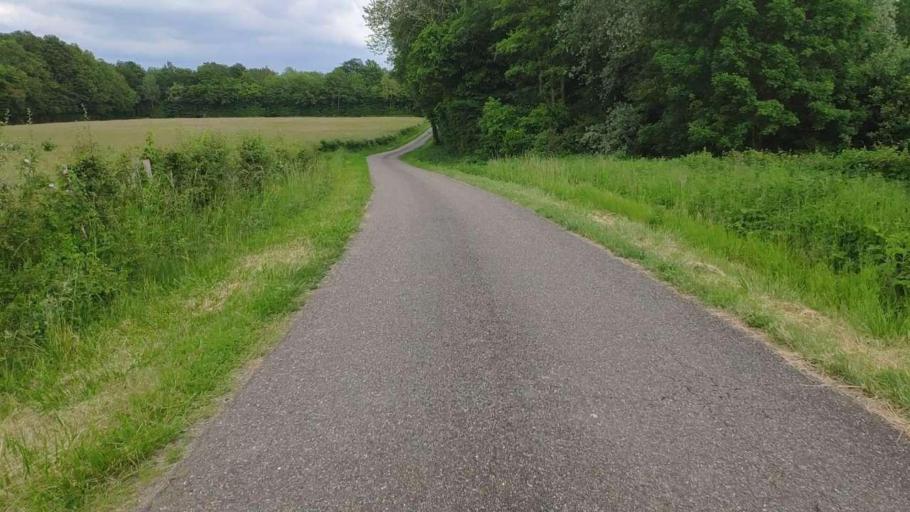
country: FR
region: Bourgogne
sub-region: Departement de Saone-et-Loire
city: Saint-Germain-du-Bois
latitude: 46.7970
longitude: 5.3487
